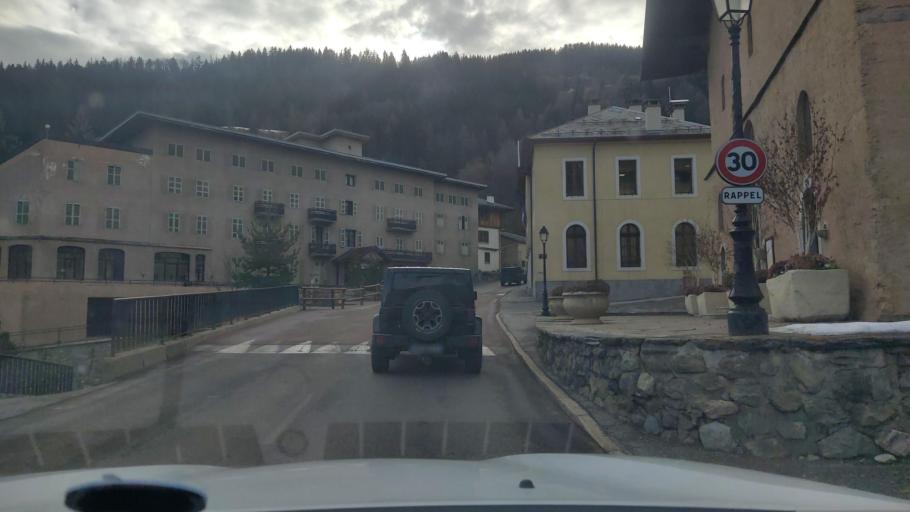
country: FR
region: Rhone-Alpes
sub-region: Departement de la Savoie
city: Saint-Bon-Tarentaise
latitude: 45.4347
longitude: 6.6374
